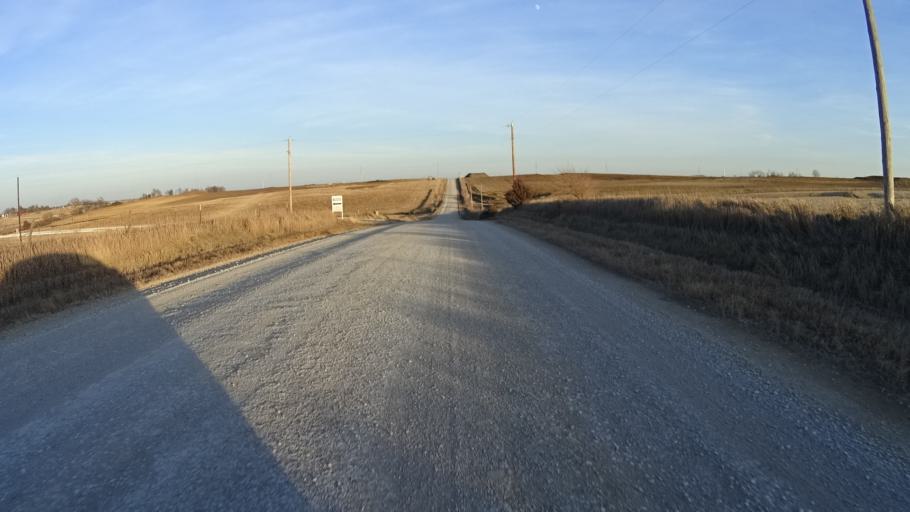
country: US
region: Nebraska
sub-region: Sarpy County
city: Springfield
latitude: 41.1326
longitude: -96.1022
